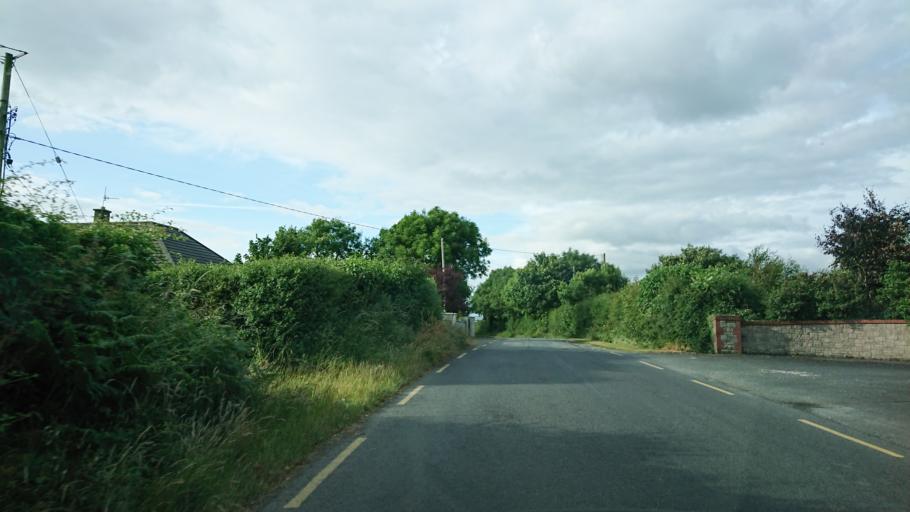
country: IE
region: Munster
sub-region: Waterford
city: Waterford
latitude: 52.2340
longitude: -7.1583
